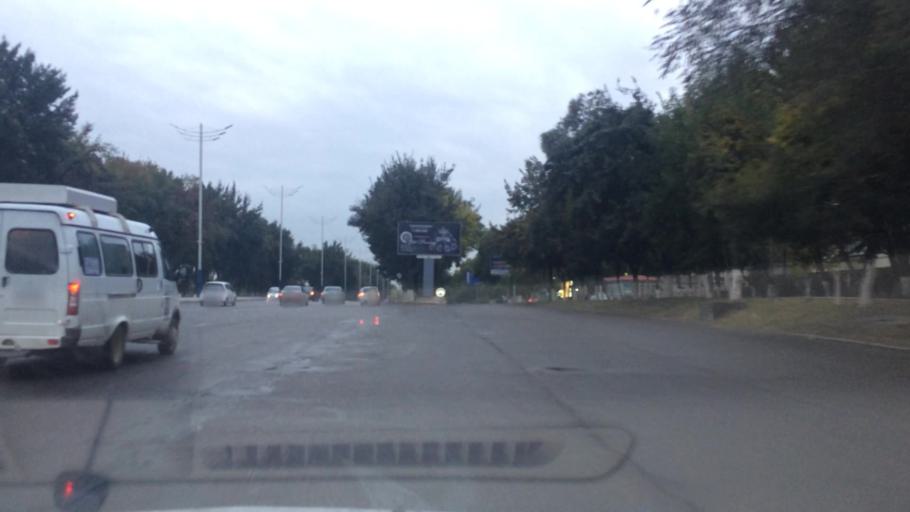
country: UZ
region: Toshkent Shahri
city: Tashkent
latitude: 41.3076
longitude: 69.2377
